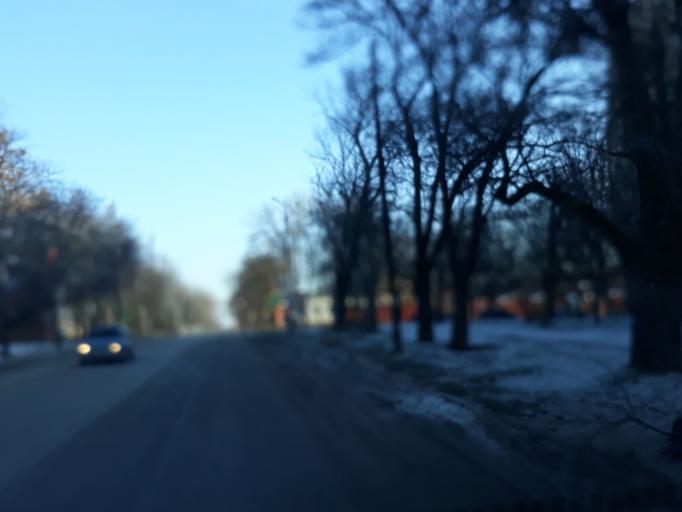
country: RU
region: Rostov
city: Taganrog
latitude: 47.2046
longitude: 38.9051
